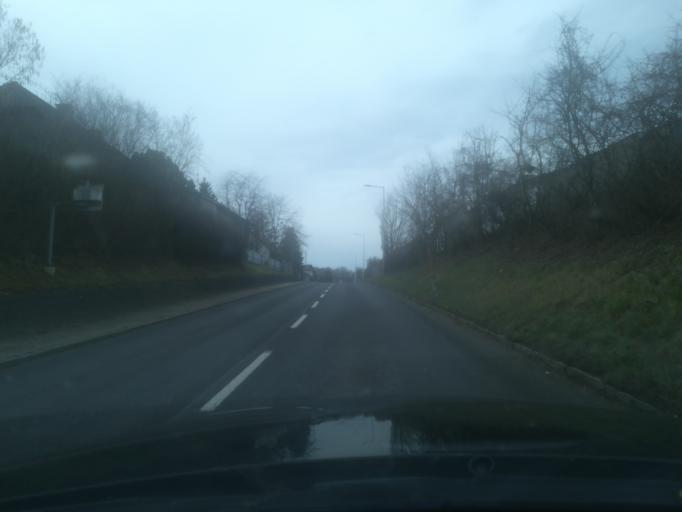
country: AT
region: Upper Austria
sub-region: Wels-Land
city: Bad Wimsbach-Neydharting
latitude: 48.0932
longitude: 13.9015
